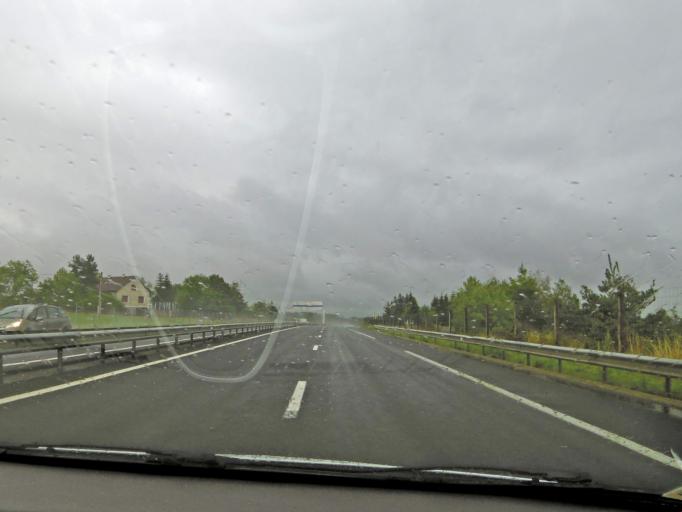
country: FR
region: Auvergne
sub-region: Departement du Cantal
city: Saint-Flour
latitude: 45.0107
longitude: 3.1573
